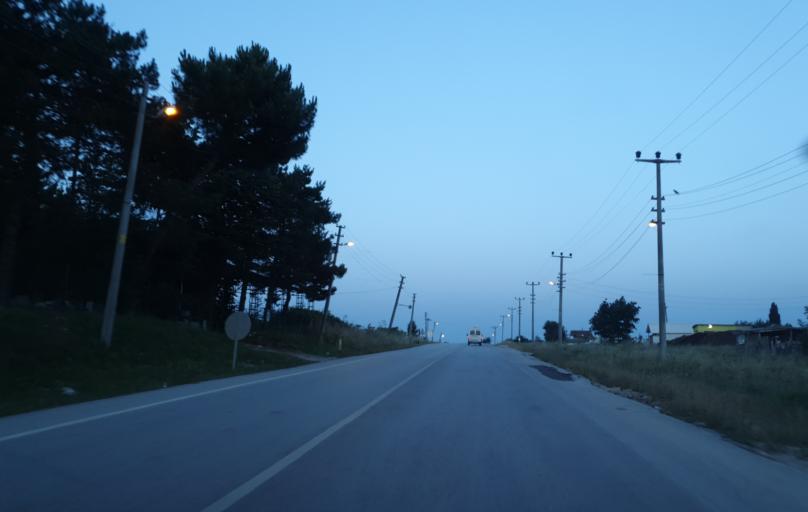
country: TR
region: Tekirdag
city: Saray
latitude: 41.3716
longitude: 27.9348
